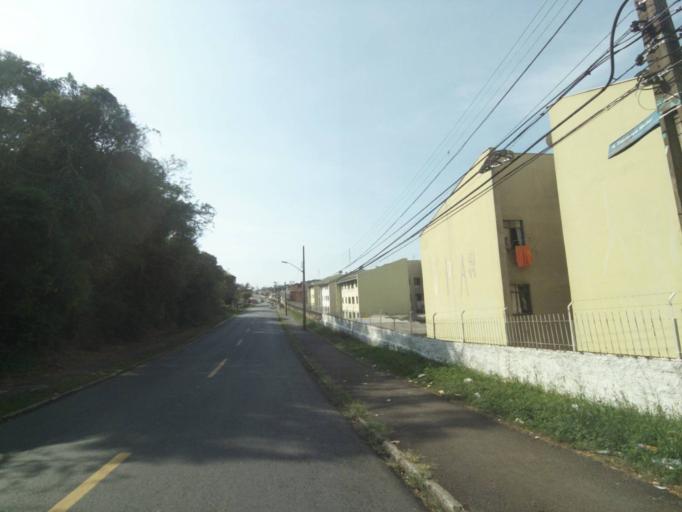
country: BR
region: Parana
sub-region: Curitiba
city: Curitiba
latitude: -25.4600
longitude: -49.3210
